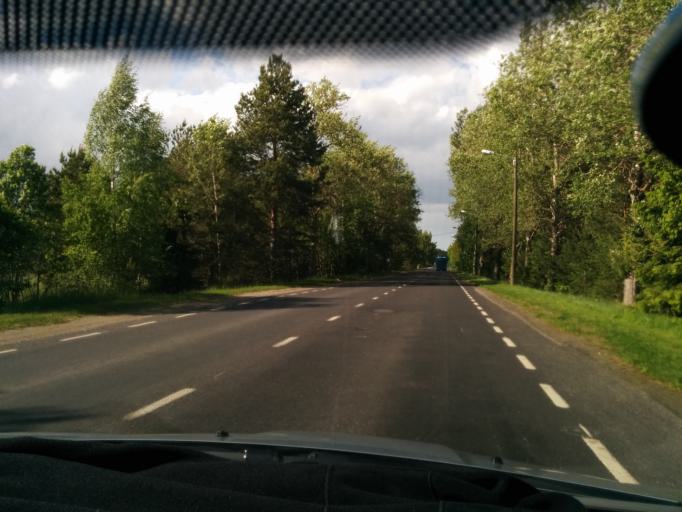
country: EE
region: Harju
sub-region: Loksa linn
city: Loksa
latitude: 59.5713
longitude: 25.7246
